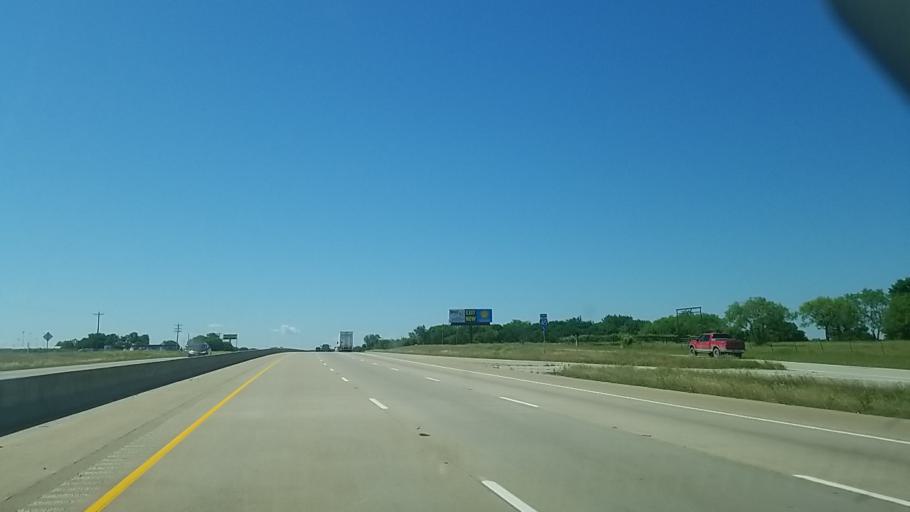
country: US
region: Texas
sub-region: Navarro County
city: Corsicana
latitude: 32.2206
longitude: -96.4844
